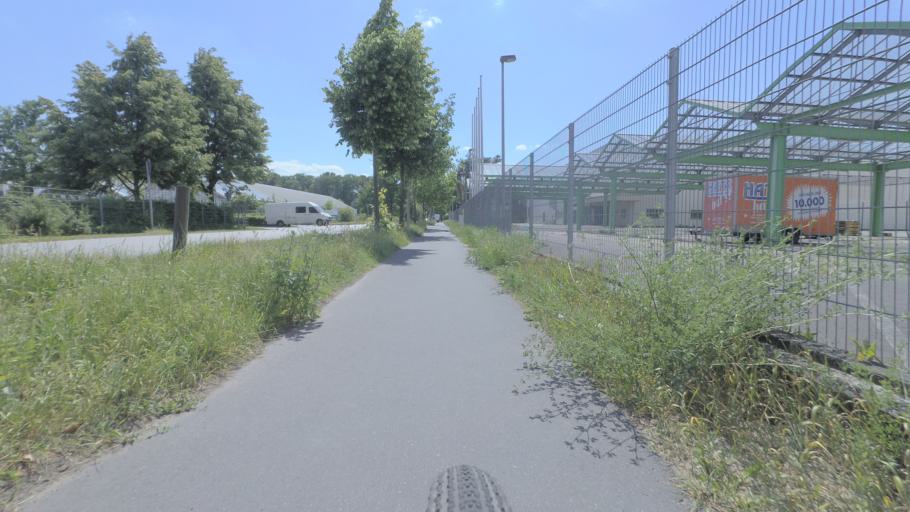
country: DE
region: Brandenburg
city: Ludwigsfelde
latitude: 52.3000
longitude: 13.2738
